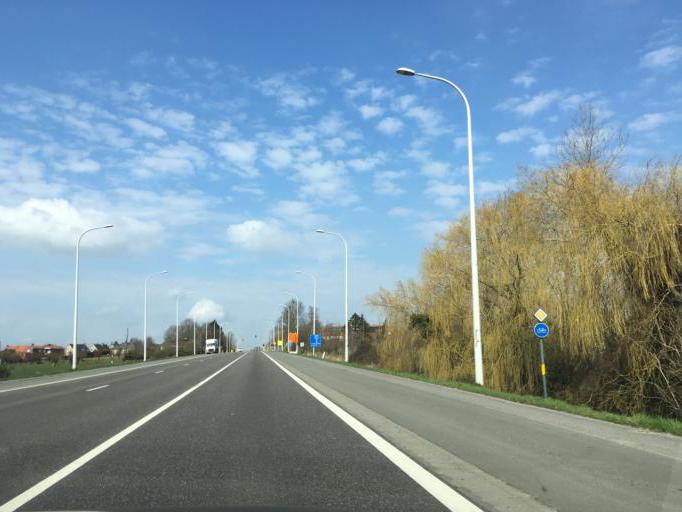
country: BE
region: Flanders
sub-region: Provincie West-Vlaanderen
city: Lendelede
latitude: 50.8847
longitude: 3.2593
